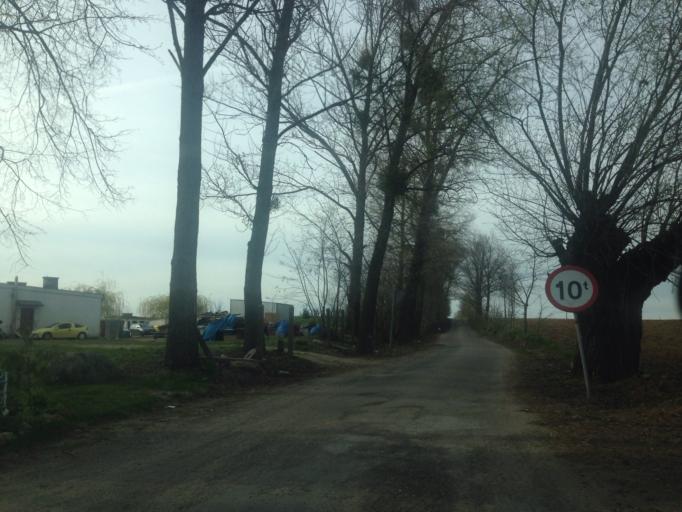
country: PL
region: Kujawsko-Pomorskie
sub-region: Powiat brodnicki
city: Jablonowo Pomorskie
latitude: 53.3998
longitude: 19.2234
